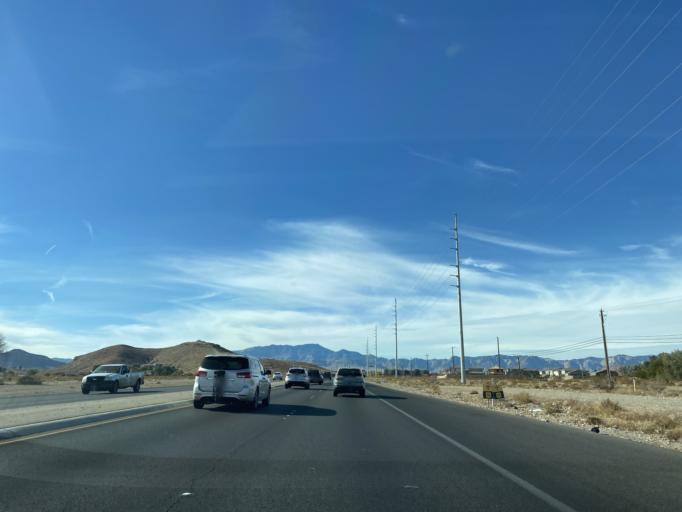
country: US
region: Nevada
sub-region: Clark County
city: Enterprise
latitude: 36.0216
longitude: -115.2482
